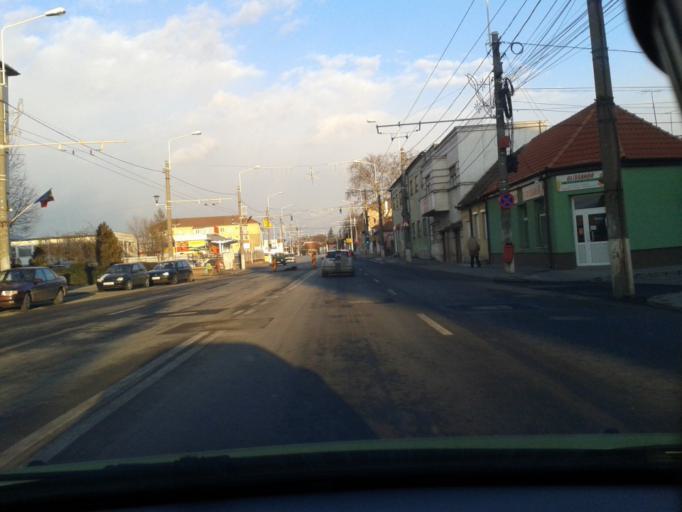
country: RO
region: Sibiu
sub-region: Municipiul Medias
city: Medias
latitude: 46.1556
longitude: 24.3409
